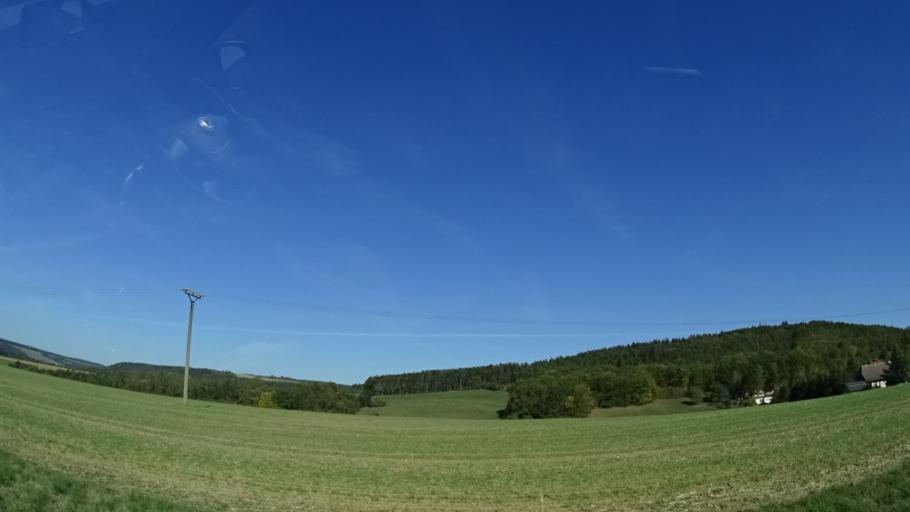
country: DE
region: Thuringia
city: Barchfeld
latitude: 50.7971
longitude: 11.1833
